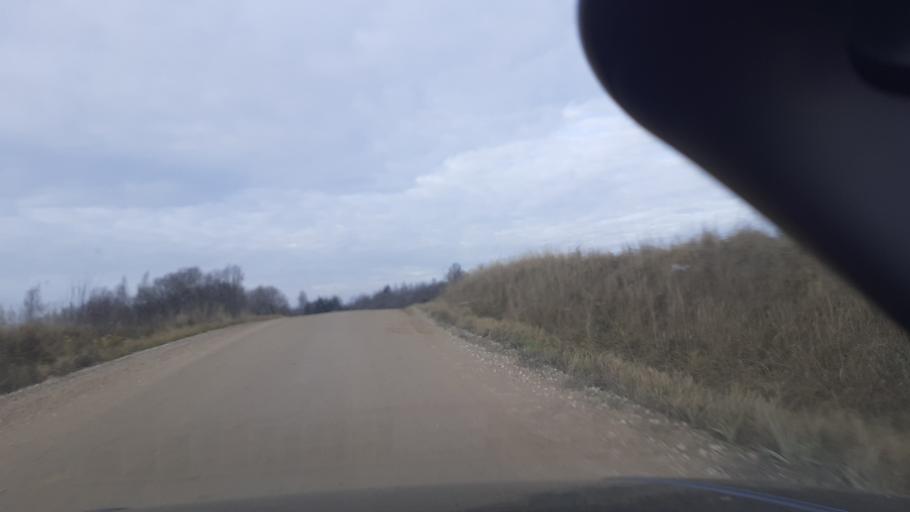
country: LV
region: Alsunga
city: Alsunga
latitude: 56.8925
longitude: 21.6638
